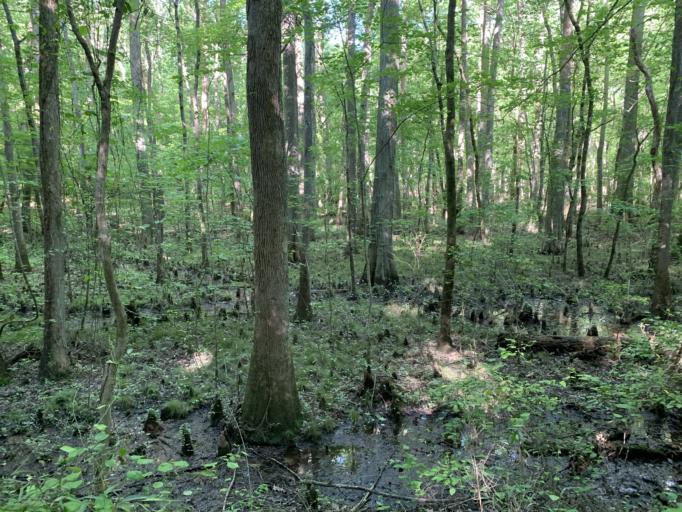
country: US
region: Tennessee
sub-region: Chester County
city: Henderson
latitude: 35.4918
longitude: -88.6784
